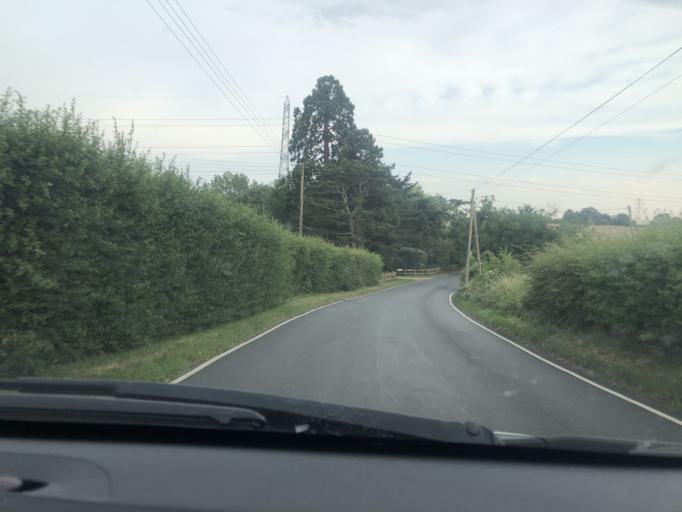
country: GB
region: England
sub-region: Kent
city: Sturry
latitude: 51.3200
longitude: 1.1434
